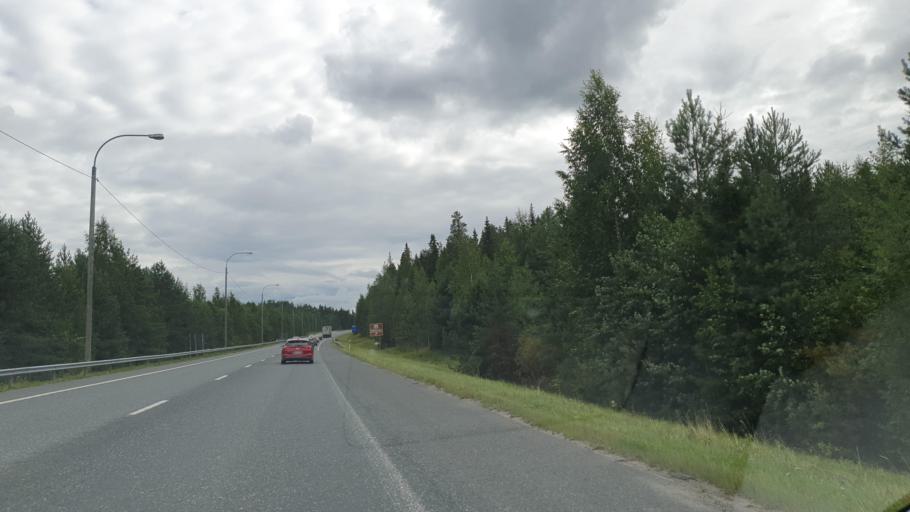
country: FI
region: Northern Savo
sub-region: Ylae-Savo
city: Iisalmi
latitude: 63.5618
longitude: 27.2550
